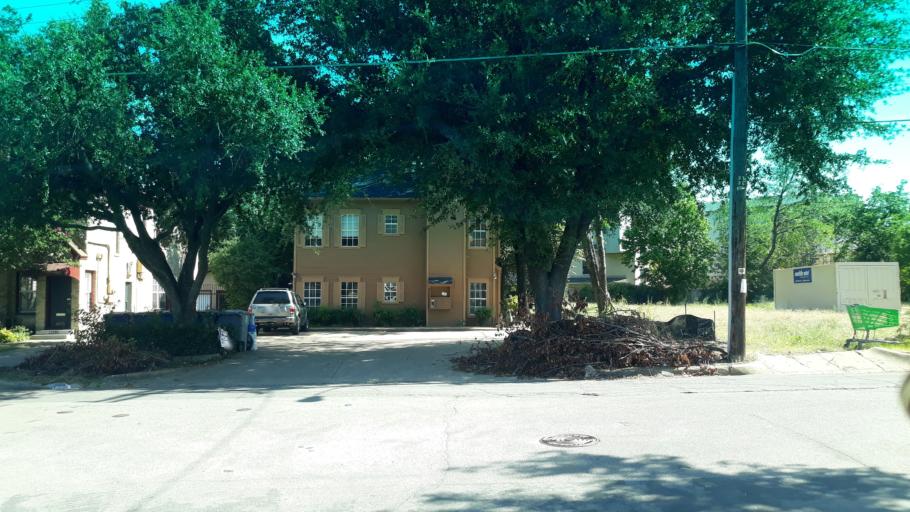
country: US
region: Texas
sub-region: Dallas County
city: Highland Park
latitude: 32.8122
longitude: -96.7628
